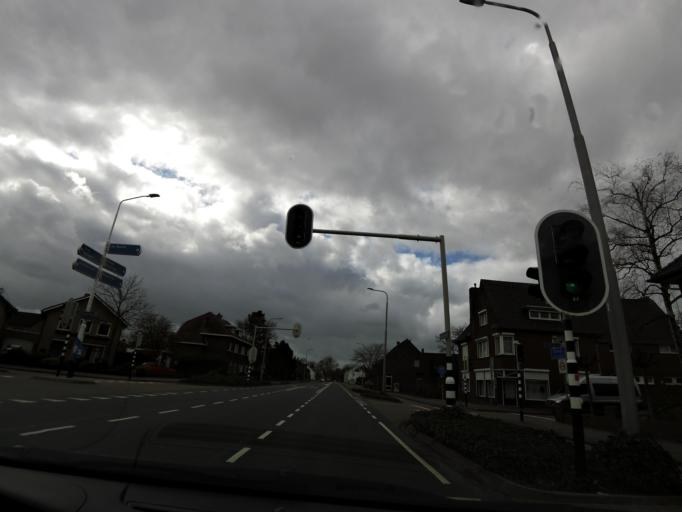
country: NL
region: Limburg
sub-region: Gemeente Venlo
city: Tegelen
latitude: 51.3326
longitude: 6.1266
